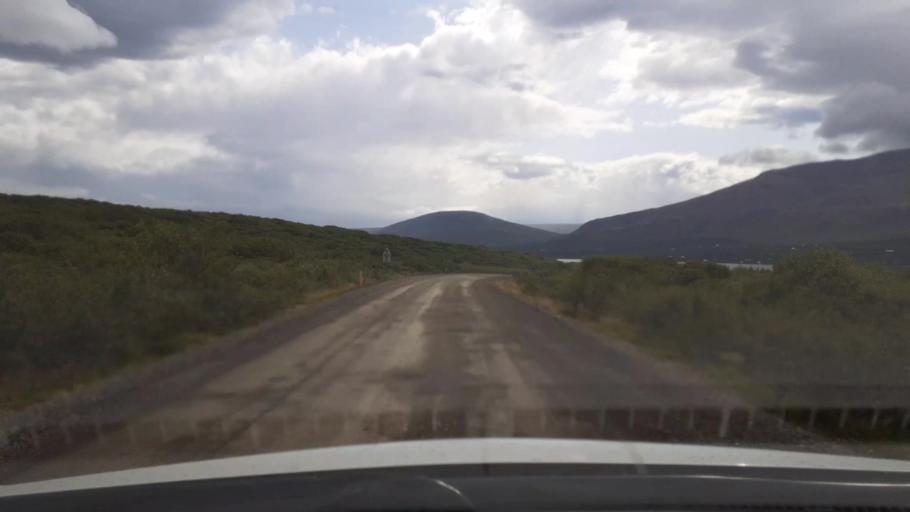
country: IS
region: West
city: Borgarnes
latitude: 64.5520
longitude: -21.6229
